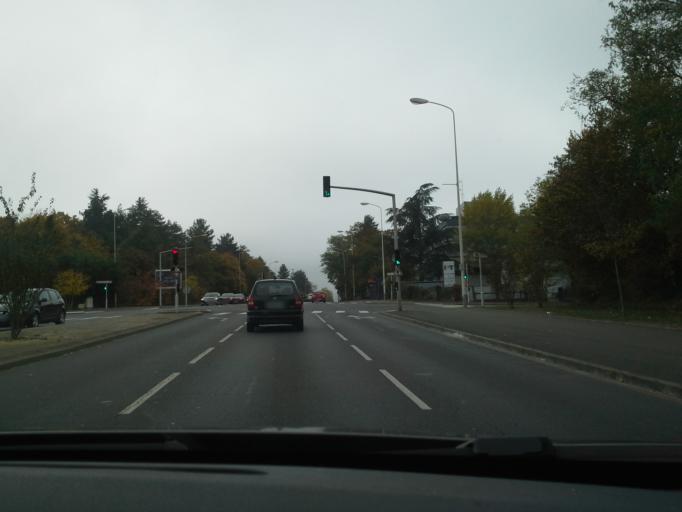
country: FR
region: Centre
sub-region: Departement d'Indre-et-Loire
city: Tours
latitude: 47.4094
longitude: 0.7033
